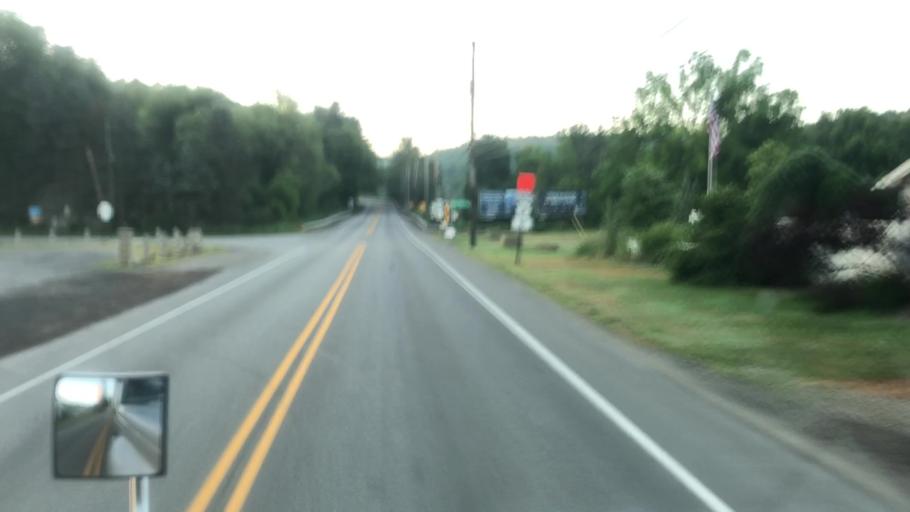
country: US
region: Pennsylvania
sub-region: Crawford County
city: Titusville
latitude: 41.6197
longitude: -79.6400
